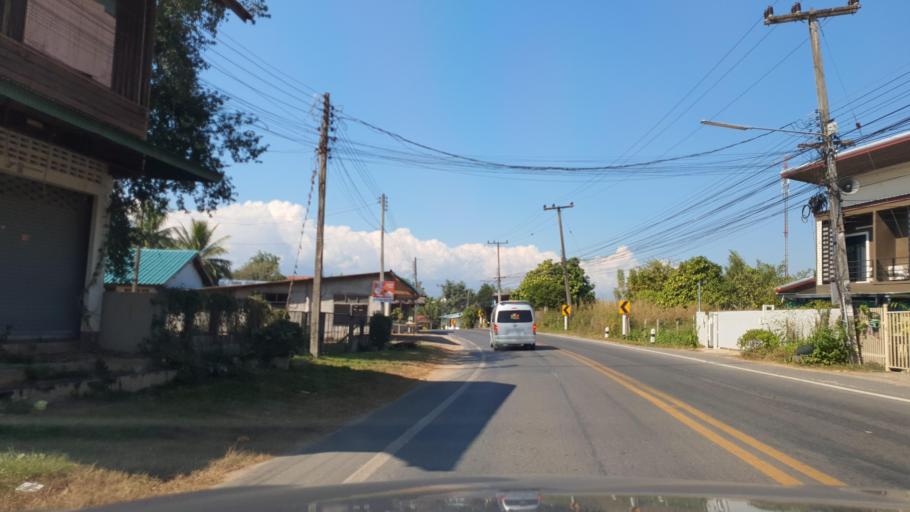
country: TH
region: Nan
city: Tha Wang Pha
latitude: 19.1058
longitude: 100.8136
